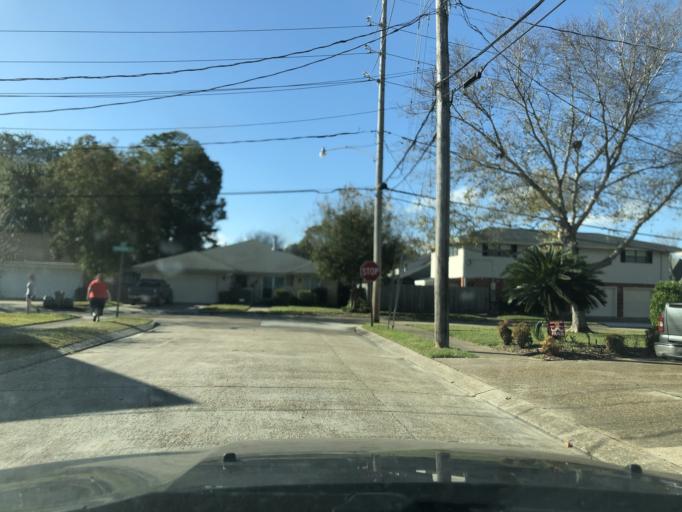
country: US
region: Louisiana
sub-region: Jefferson Parish
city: Metairie Terrace
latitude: 29.9913
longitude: -90.1641
